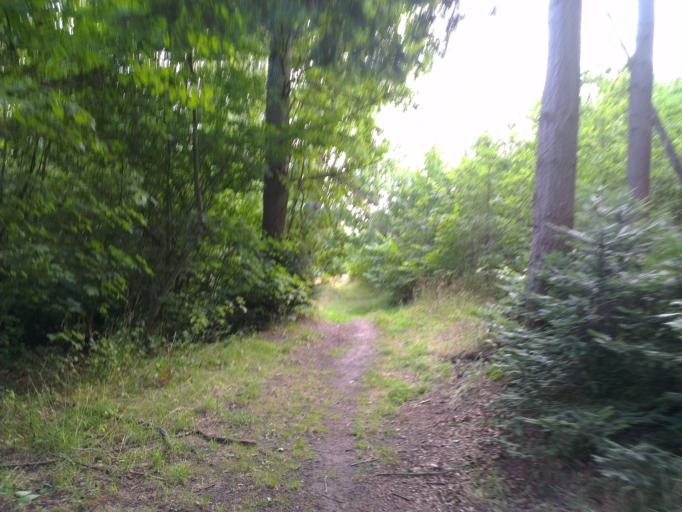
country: DK
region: Capital Region
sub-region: Frederikssund Kommune
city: Frederikssund
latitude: 55.8488
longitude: 12.0278
